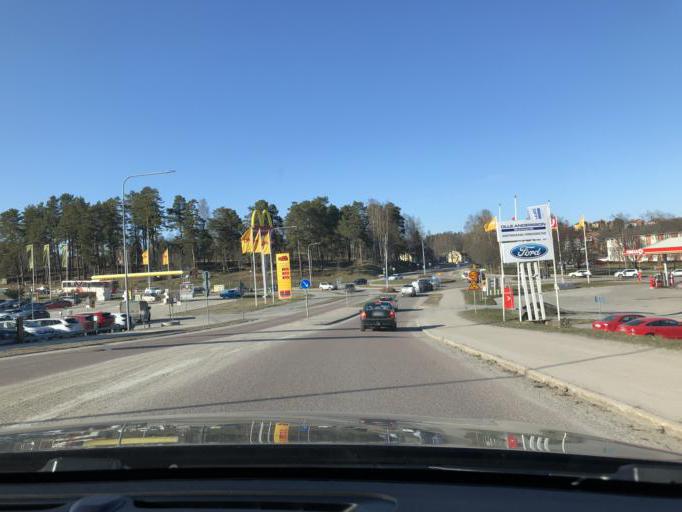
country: SE
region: Gaevleborg
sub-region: Hudiksvalls Kommun
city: Hudiksvall
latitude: 61.7332
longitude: 17.1000
